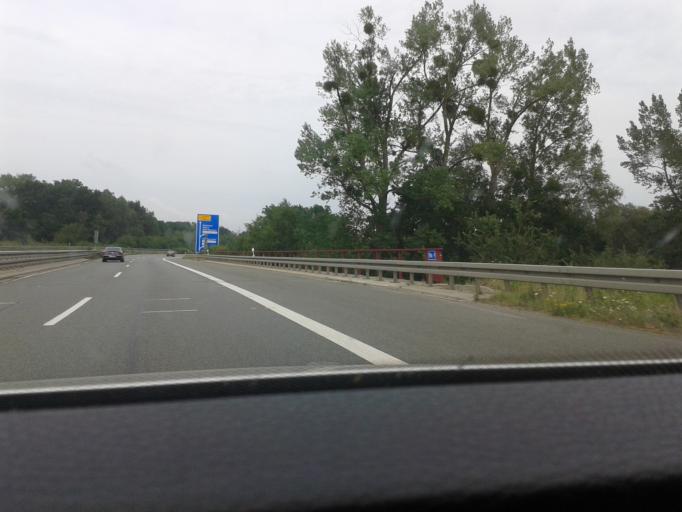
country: DE
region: Lower Saxony
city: Tappenbeck
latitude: 52.4535
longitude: 10.7380
